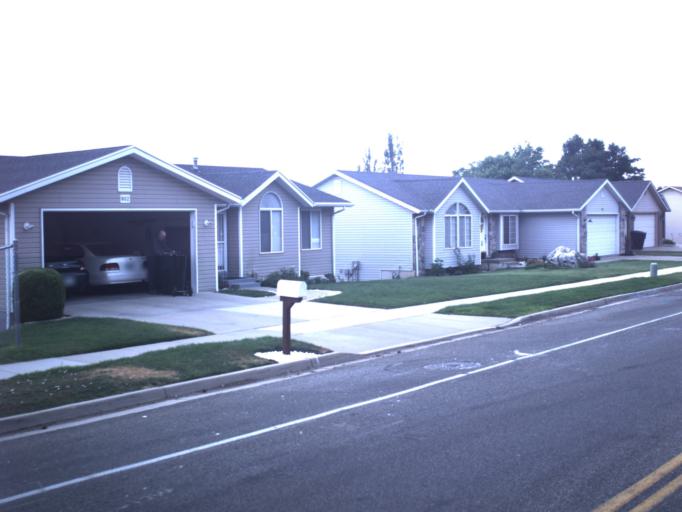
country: US
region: Utah
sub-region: Davis County
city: Farmington
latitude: 40.9654
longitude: -111.8834
